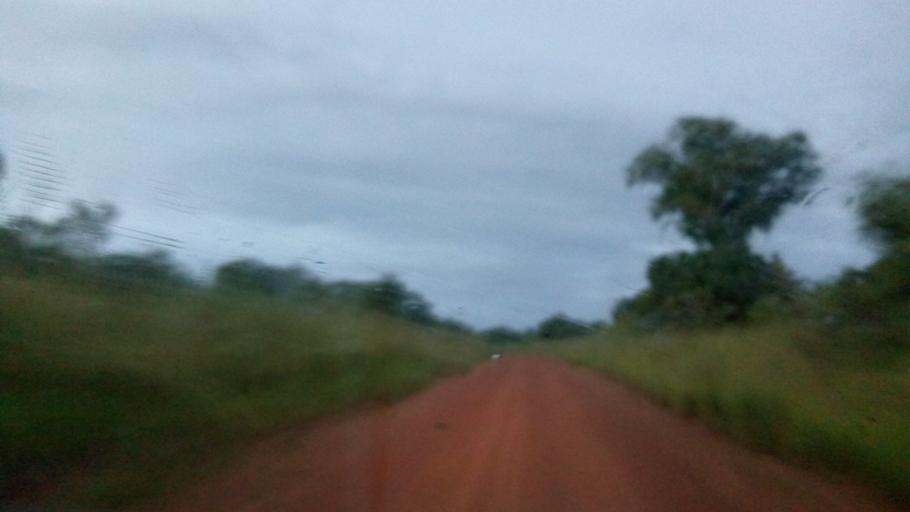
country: ZM
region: Luapula
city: Nchelenge
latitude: -9.8341
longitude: 28.1301
